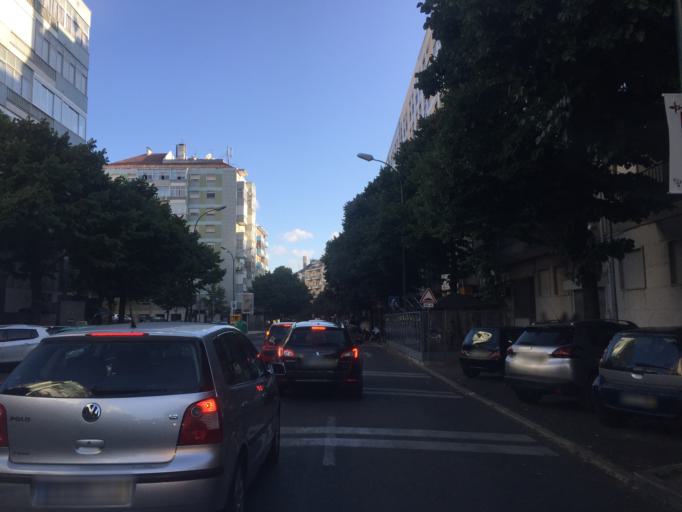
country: PT
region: Lisbon
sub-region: Odivelas
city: Pontinha
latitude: 38.7532
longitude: -9.1965
